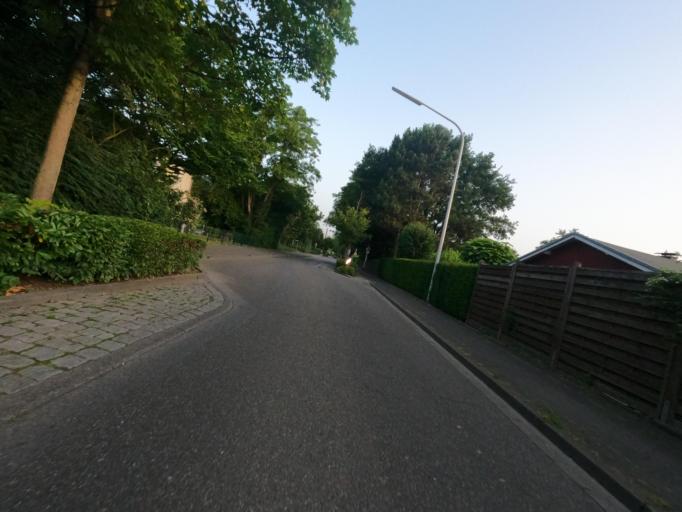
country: DE
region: North Rhine-Westphalia
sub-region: Regierungsbezirk Koln
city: Wassenberg
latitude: 51.0559
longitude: 6.1529
